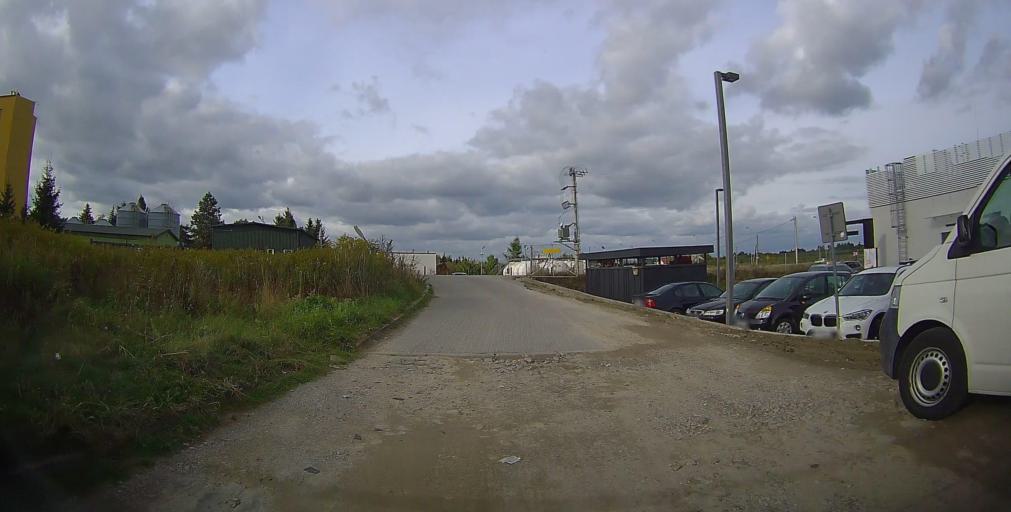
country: PL
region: Masovian Voivodeship
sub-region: Powiat bialobrzeski
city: Promna
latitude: 51.6997
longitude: 20.9345
